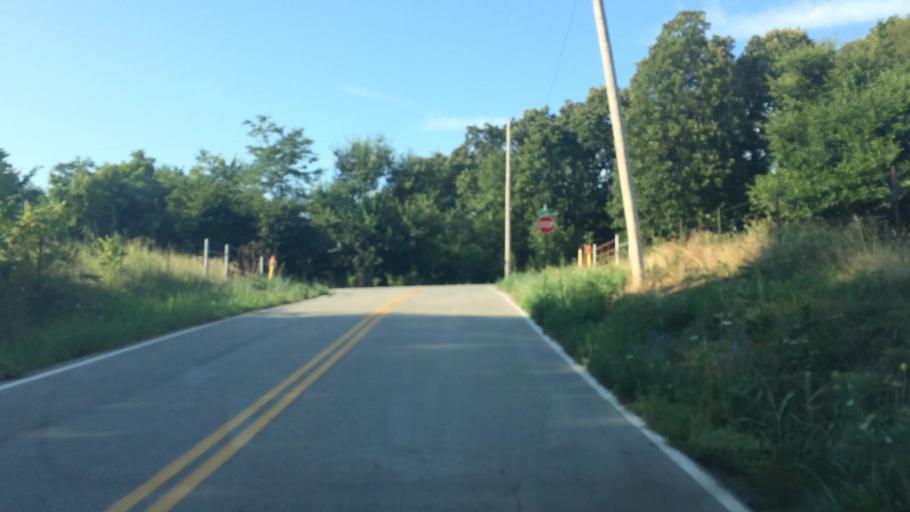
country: US
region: Missouri
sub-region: Greene County
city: Strafford
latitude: 37.2565
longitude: -93.1879
